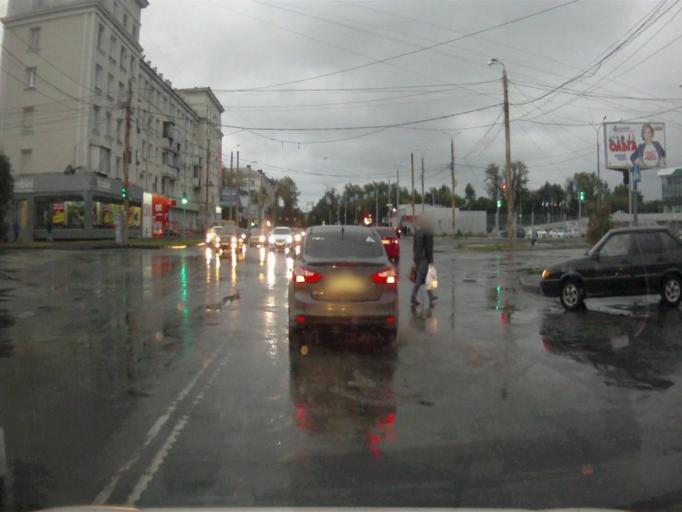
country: RU
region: Chelyabinsk
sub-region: Gorod Chelyabinsk
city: Chelyabinsk
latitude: 55.1628
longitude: 61.4339
